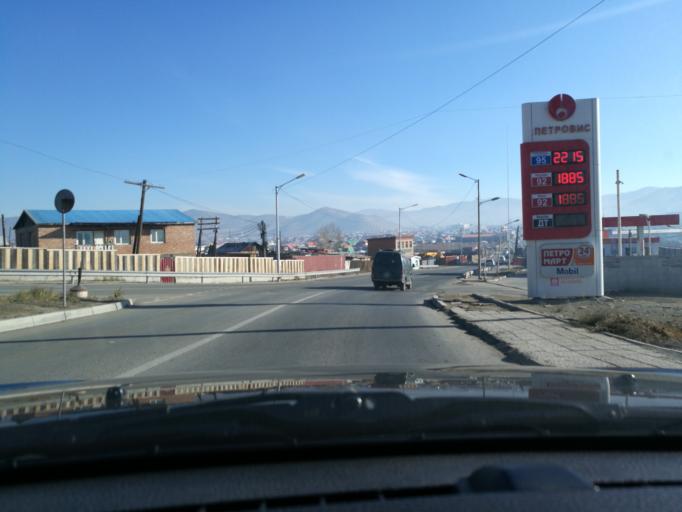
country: MN
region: Ulaanbaatar
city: Ulaanbaatar
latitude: 47.9755
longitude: 106.9187
